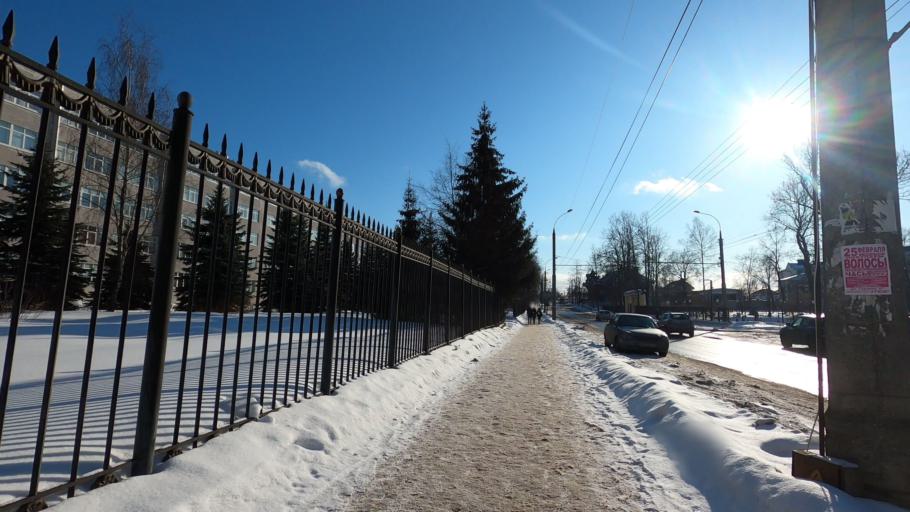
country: RU
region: Jaroslavl
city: Rybinsk
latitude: 58.0454
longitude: 38.8382
